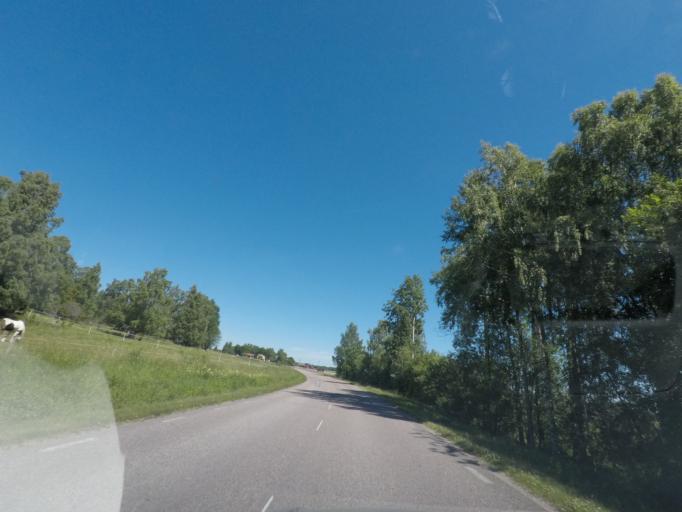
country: SE
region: Vaestmanland
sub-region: Vasteras
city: Tillberga
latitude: 59.6406
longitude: 16.6782
